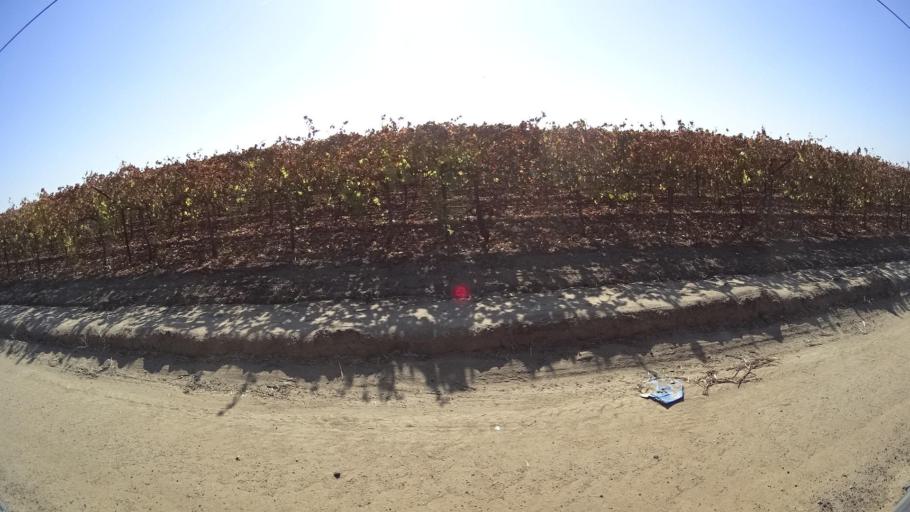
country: US
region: California
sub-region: Kern County
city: McFarland
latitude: 35.7178
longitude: -119.1946
